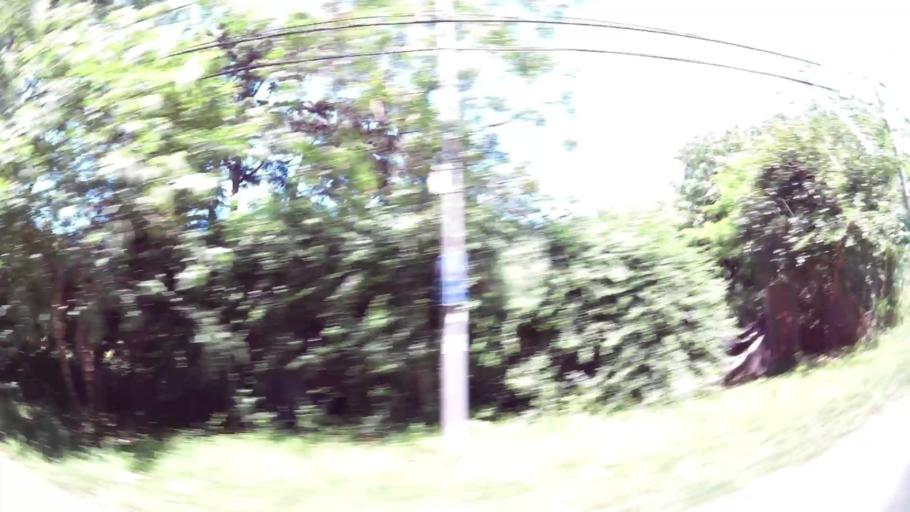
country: AR
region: Buenos Aires
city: Hurlingham
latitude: -34.4983
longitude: -58.6345
